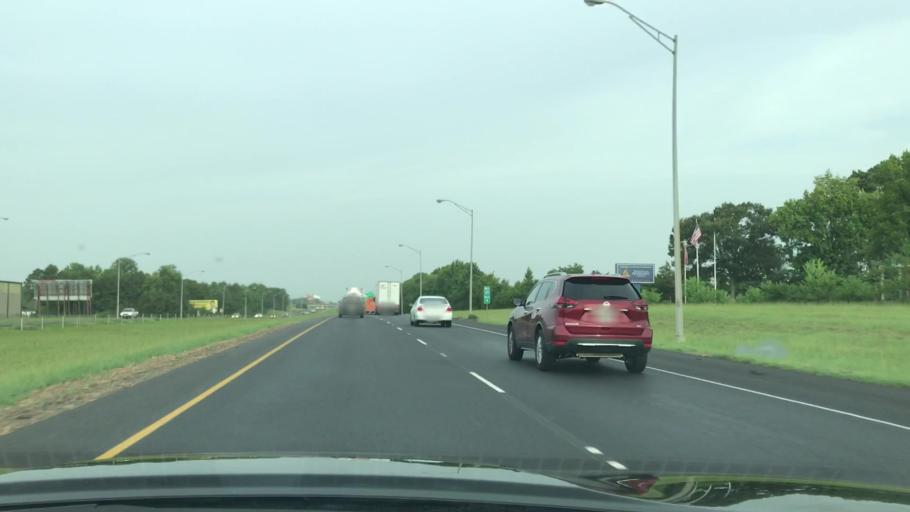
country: US
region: Louisiana
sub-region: Caddo Parish
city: Greenwood
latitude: 32.4486
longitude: -93.8885
